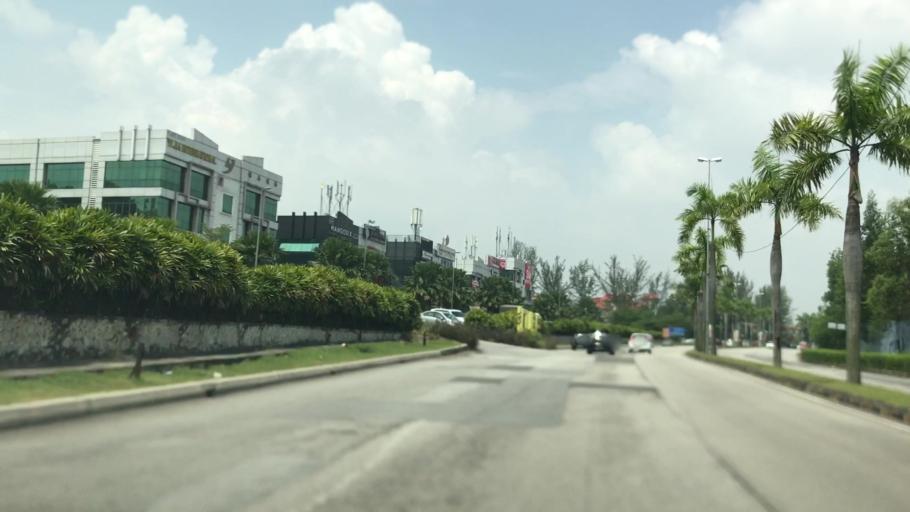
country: MY
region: Selangor
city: Subang Jaya
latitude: 3.0199
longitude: 101.6246
